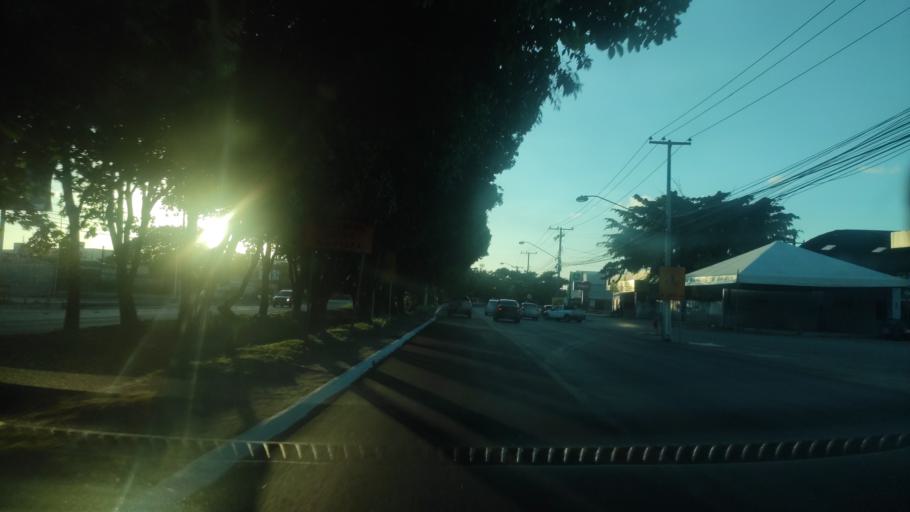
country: BR
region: Alagoas
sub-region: Satuba
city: Satuba
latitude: -9.5912
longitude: -35.7585
